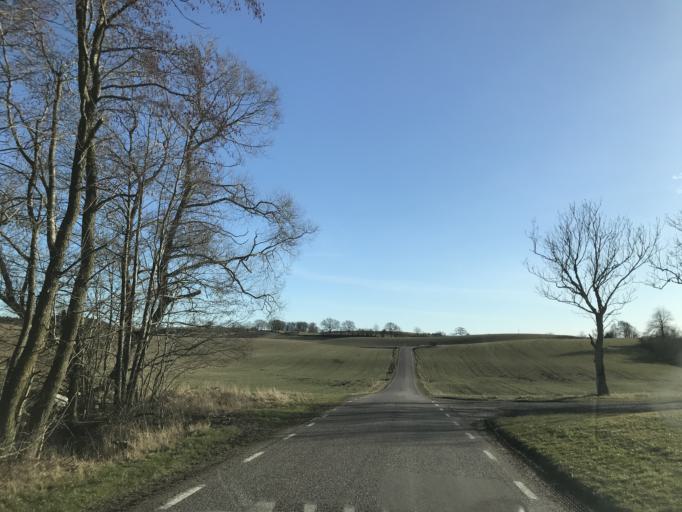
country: SE
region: Skane
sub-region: Ystads Kommun
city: Ystad
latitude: 55.5397
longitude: 13.7873
